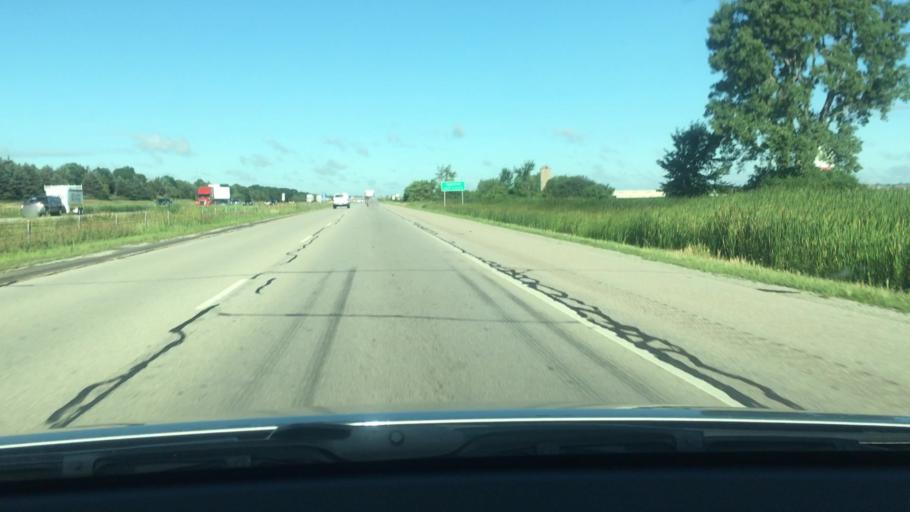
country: US
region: Wisconsin
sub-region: Outagamie County
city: Little Chute
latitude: 44.2981
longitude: -88.3340
